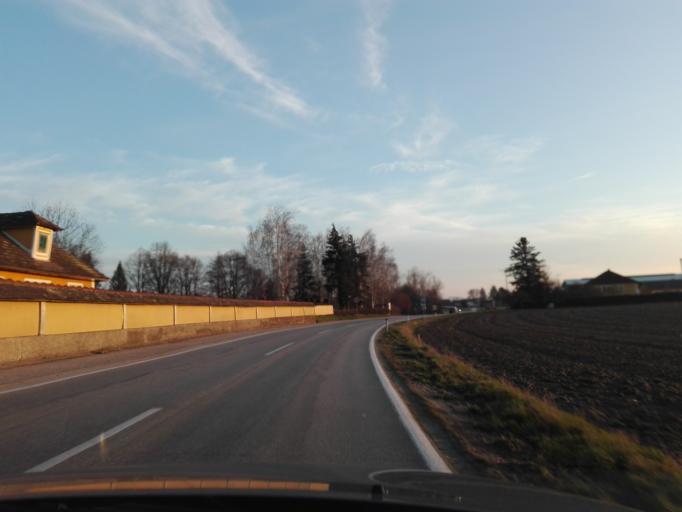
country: AT
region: Upper Austria
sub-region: Politischer Bezirk Urfahr-Umgebung
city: Feldkirchen an der Donau
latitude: 48.3232
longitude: 14.0126
